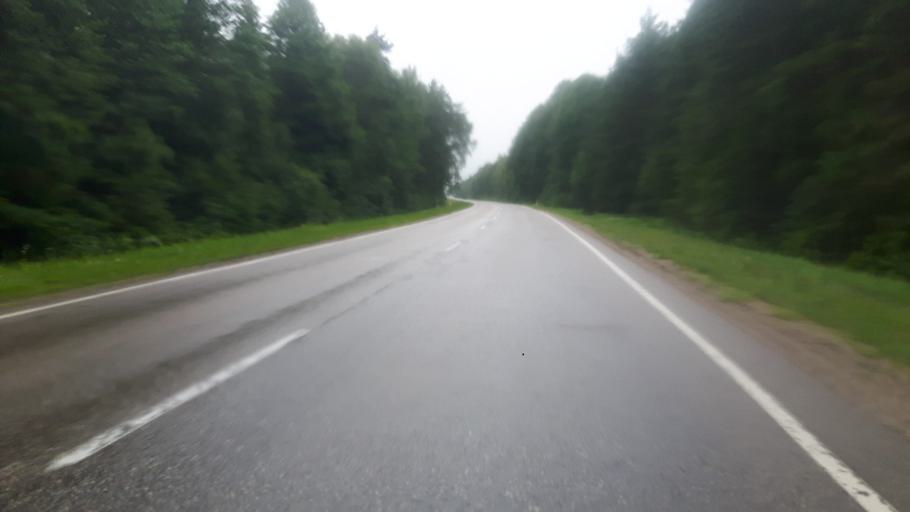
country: LV
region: Rucavas
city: Rucava
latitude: 56.1391
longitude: 21.1523
